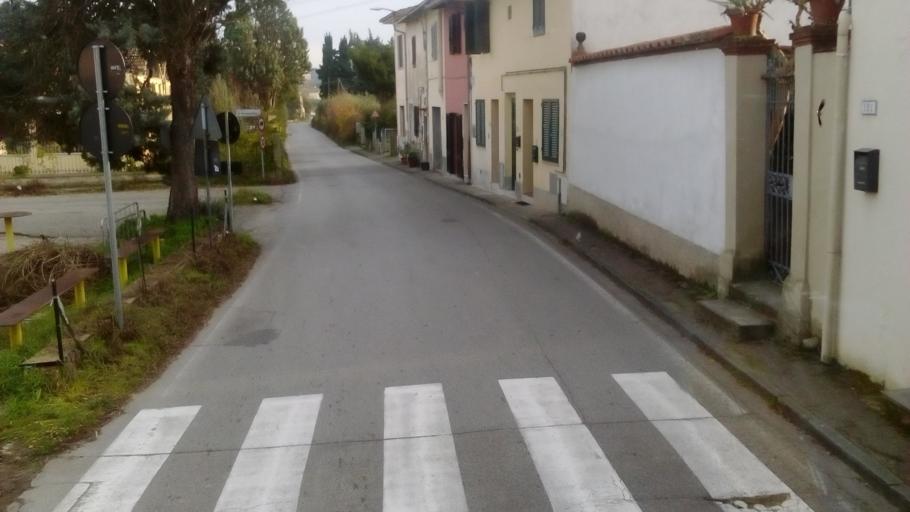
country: IT
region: Tuscany
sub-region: Province of Florence
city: Montelupo Fiorentino
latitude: 43.7055
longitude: 10.9924
